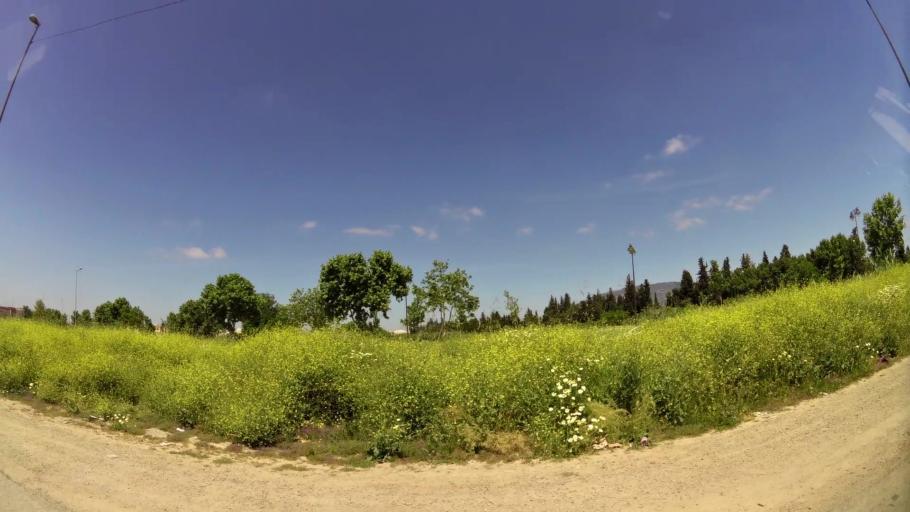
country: MA
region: Fes-Boulemane
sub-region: Fes
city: Fes
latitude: 34.0280
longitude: -5.0180
